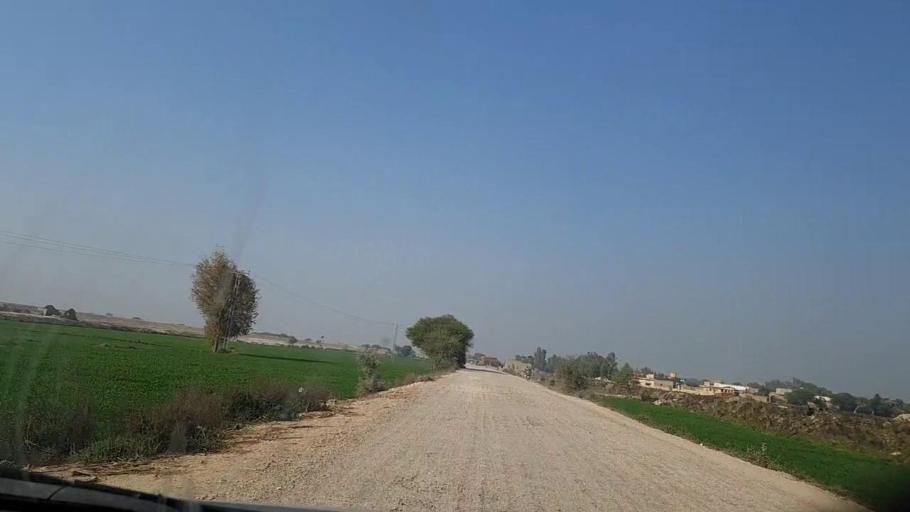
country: PK
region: Sindh
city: Moro
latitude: 26.7364
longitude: 67.9195
